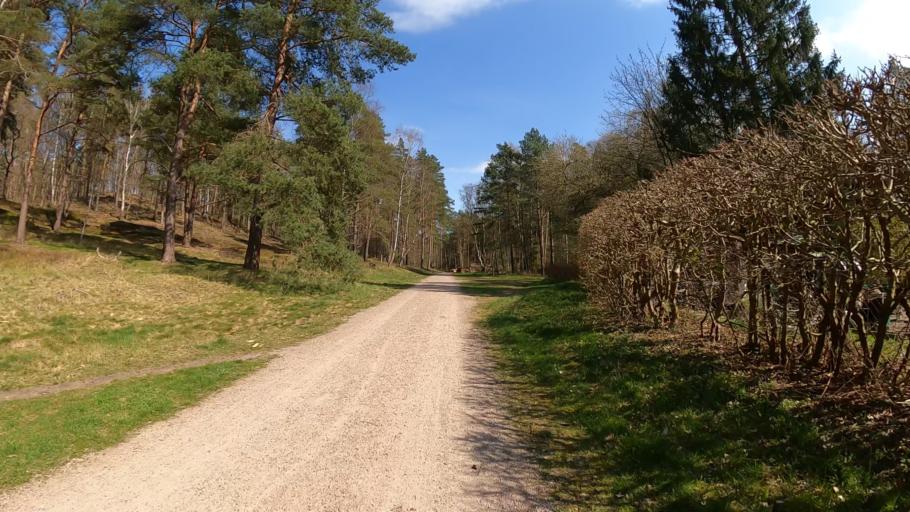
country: DE
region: Lower Saxony
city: Neu Wulmstorf
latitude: 53.4583
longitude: 9.8671
